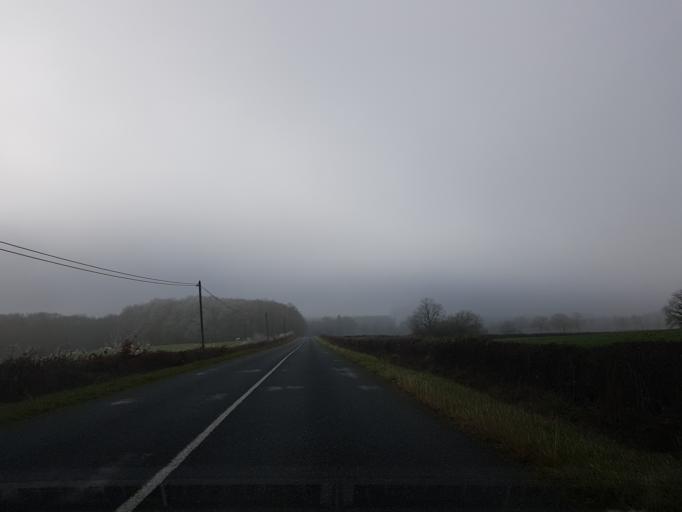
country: FR
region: Bourgogne
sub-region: Departement de Saone-et-Loire
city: Toulon-sur-Arroux
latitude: 46.6979
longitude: 4.1925
